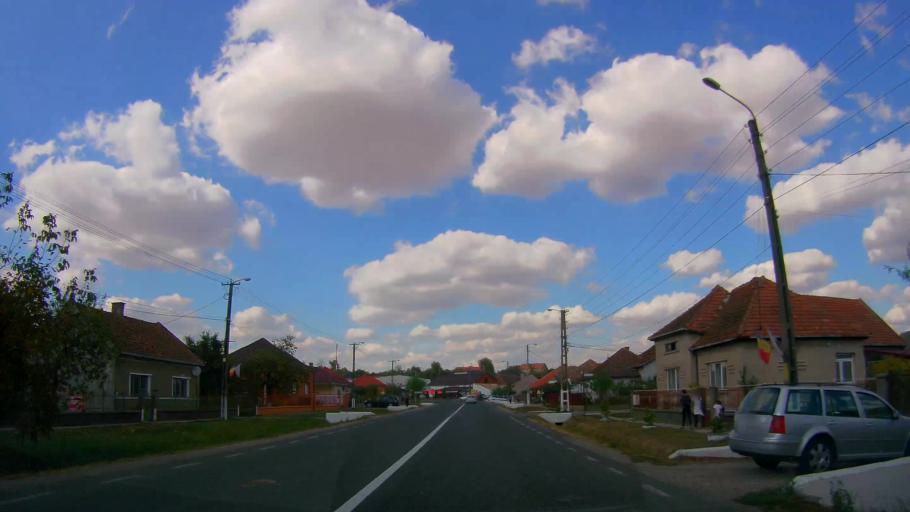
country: RO
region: Satu Mare
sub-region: Oras Ardud
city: Ardud
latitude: 47.6489
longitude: 22.8914
